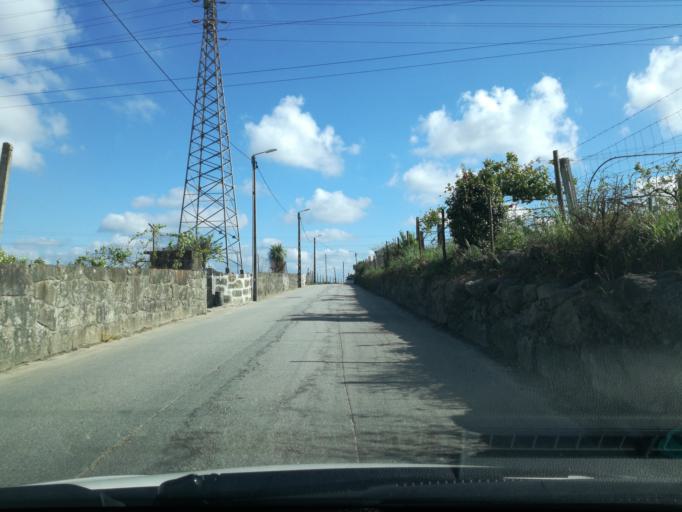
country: PT
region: Porto
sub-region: Valongo
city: Ermesinde
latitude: 41.2333
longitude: -8.5618
